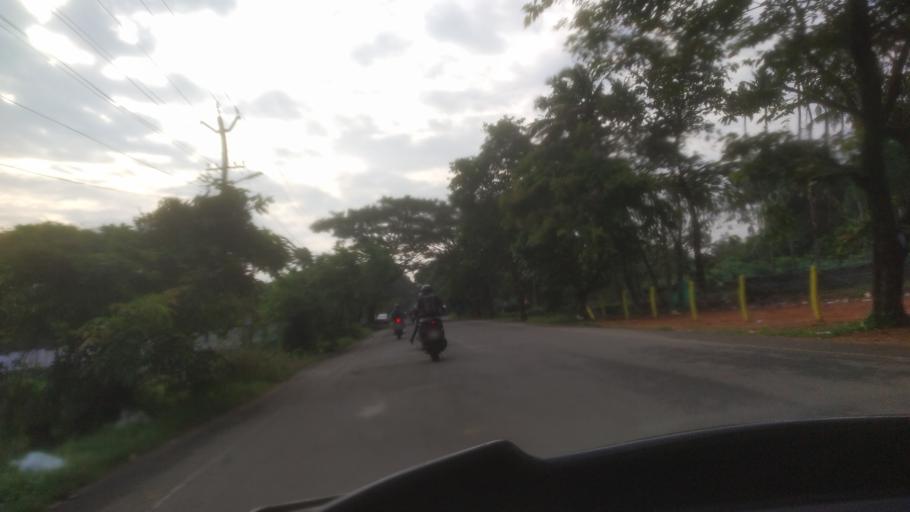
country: IN
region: Kerala
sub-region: Ernakulam
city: Kotamangalam
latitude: 10.0637
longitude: 76.6328
